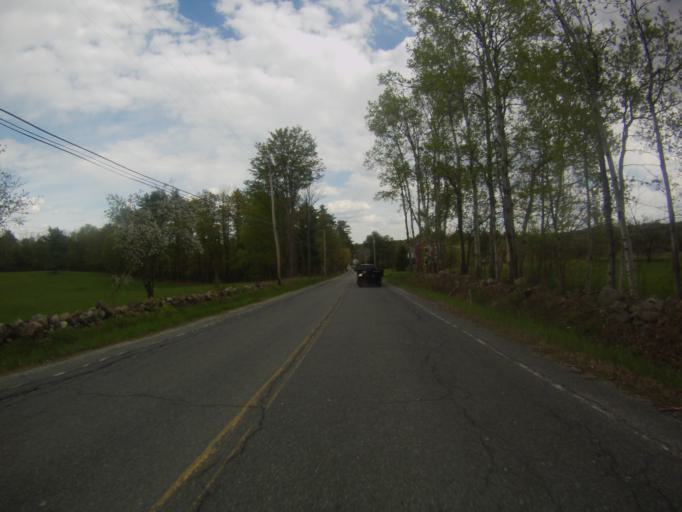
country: US
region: New York
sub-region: Essex County
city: Mineville
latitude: 44.0663
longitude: -73.5162
